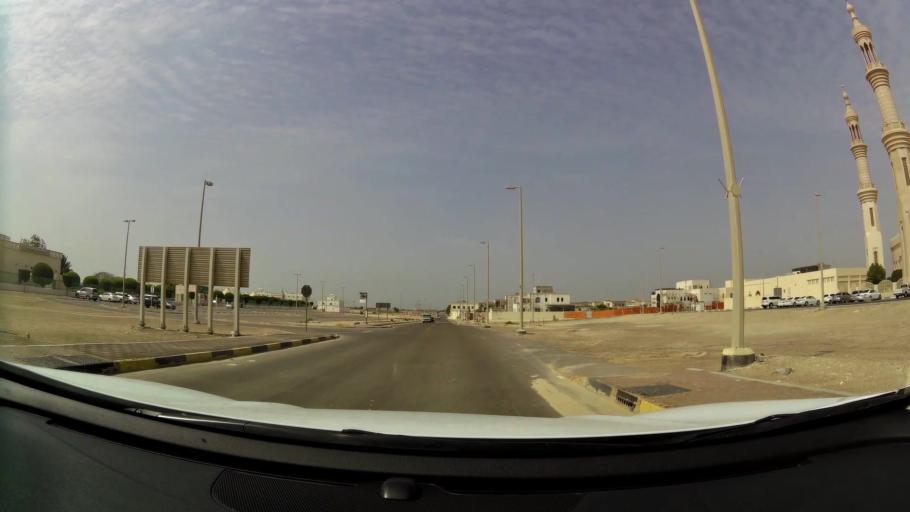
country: AE
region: Abu Dhabi
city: Abu Dhabi
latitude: 24.5148
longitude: 54.6648
